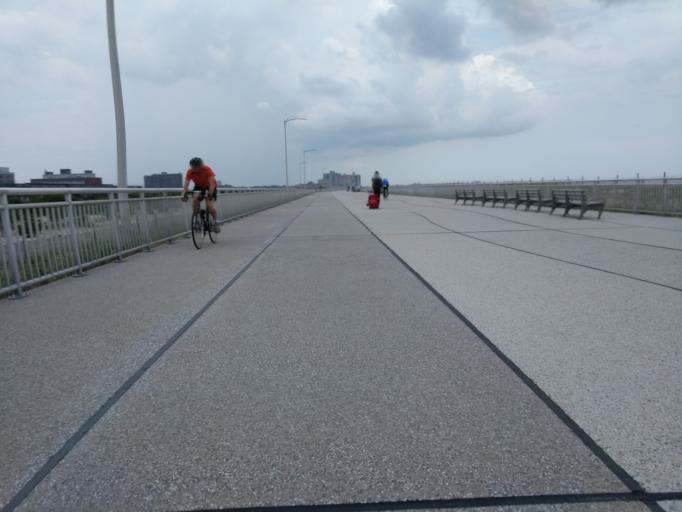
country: US
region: New York
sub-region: Nassau County
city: Inwood
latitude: 40.5911
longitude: -73.7793
